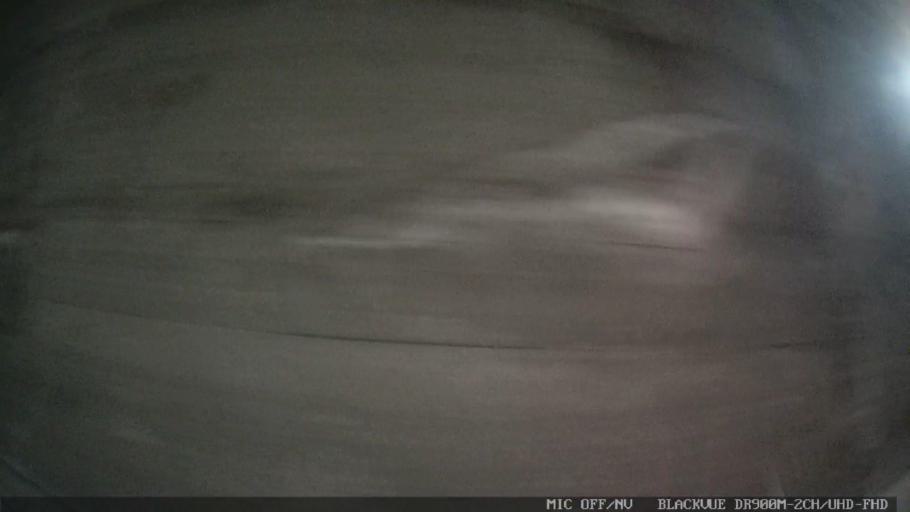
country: BR
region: Sao Paulo
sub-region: Cubatao
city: Cubatao
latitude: -23.8915
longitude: -46.5060
